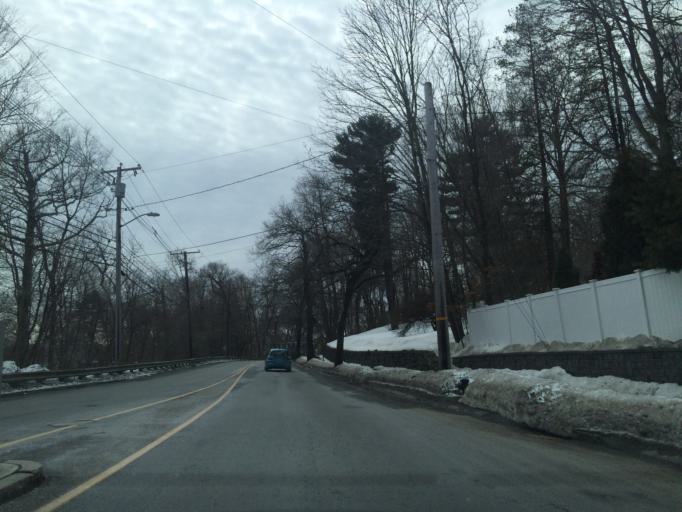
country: US
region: Massachusetts
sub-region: Middlesex County
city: Lexington
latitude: 42.4403
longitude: -71.2330
